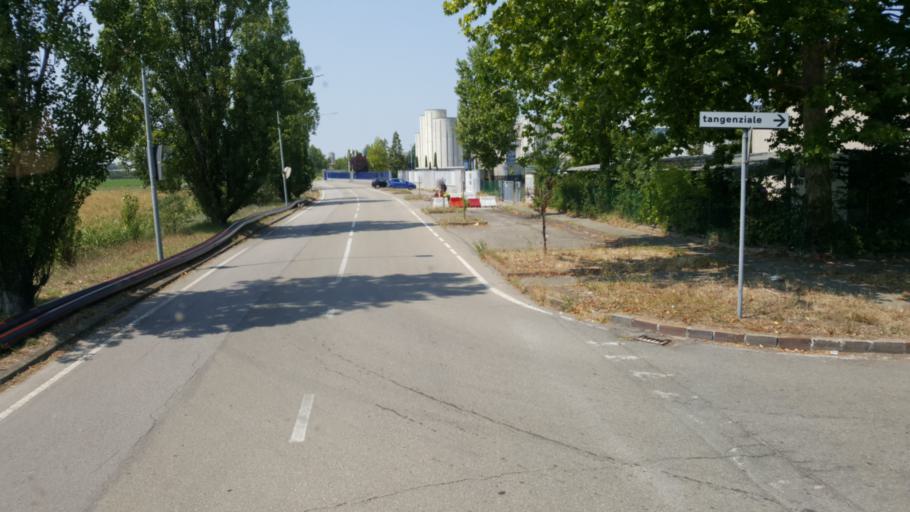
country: IT
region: Emilia-Romagna
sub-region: Provincia di Modena
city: Modena
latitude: 44.6475
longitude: 10.9599
